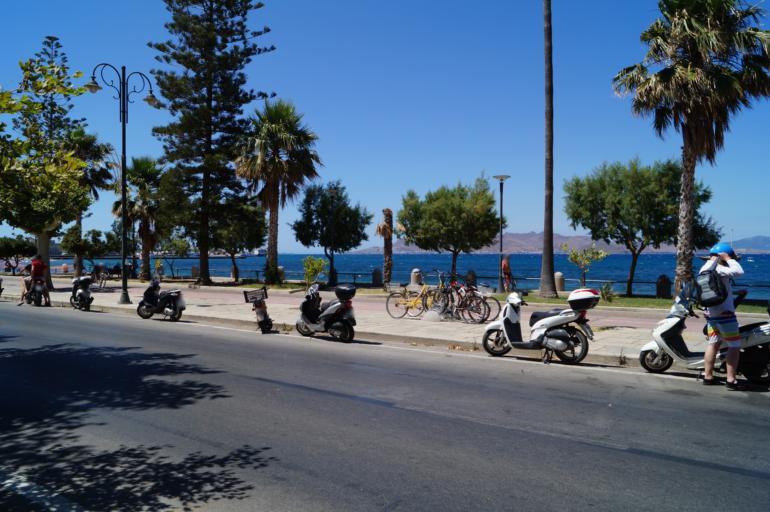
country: GR
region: South Aegean
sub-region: Nomos Dodekanisou
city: Kos
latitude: 36.8927
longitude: 27.2946
